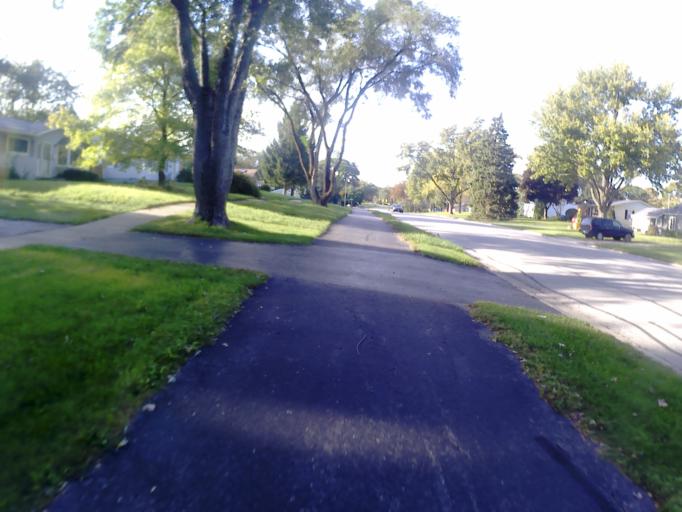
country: US
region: Illinois
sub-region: DuPage County
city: Woodridge
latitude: 41.7464
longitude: -88.0501
